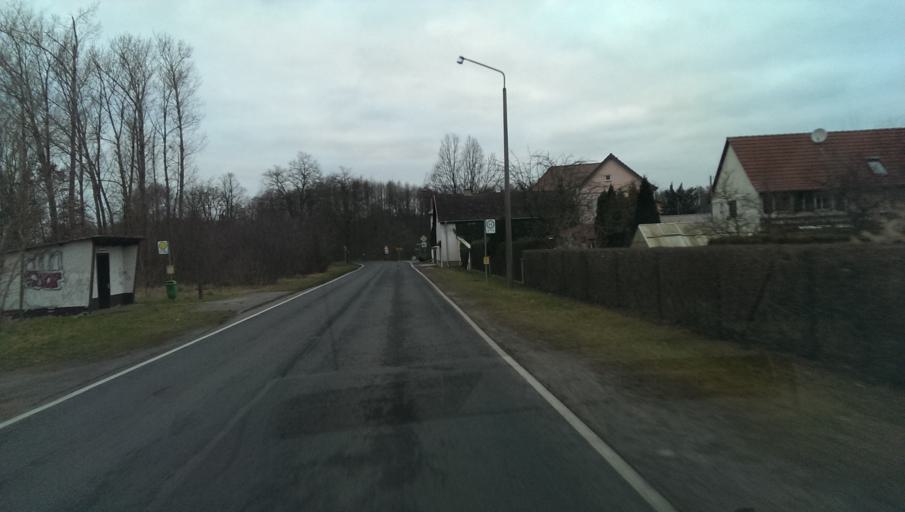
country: DE
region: Brandenburg
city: Sperenberg
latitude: 52.1576
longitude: 13.3457
